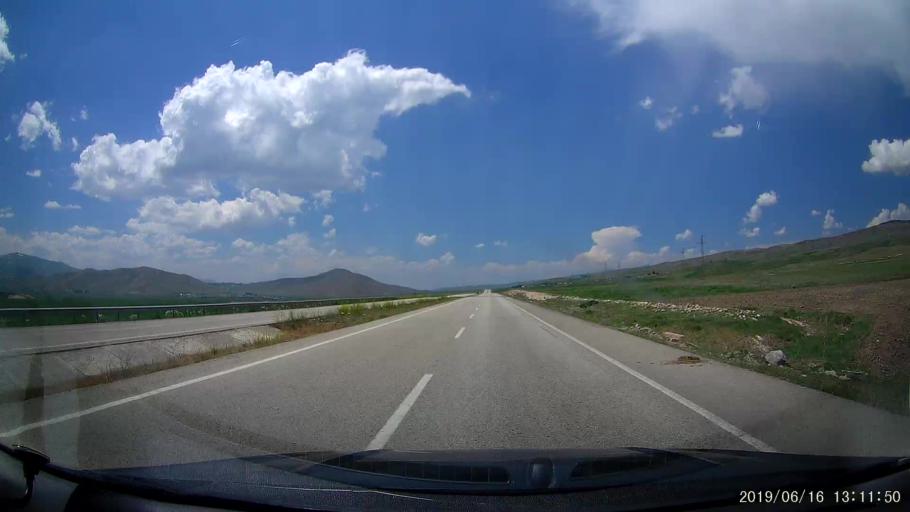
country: TR
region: Agri
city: Diyadin
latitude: 39.5943
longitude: 43.5963
